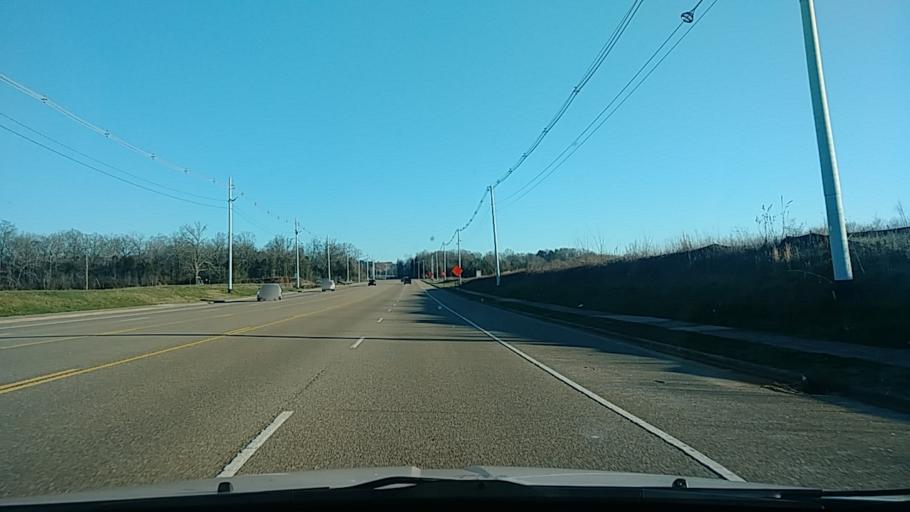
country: US
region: Tennessee
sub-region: Hamblen County
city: Morristown
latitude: 36.1851
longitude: -83.3555
